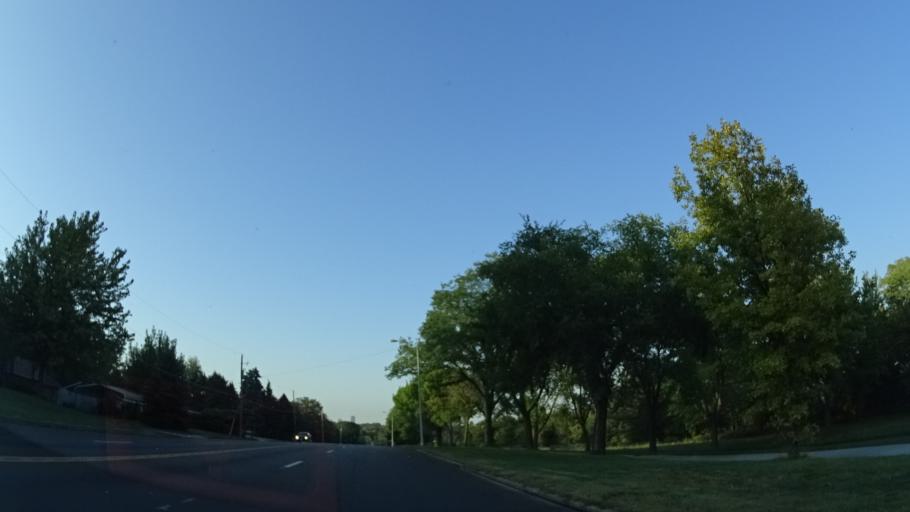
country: US
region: Nebraska
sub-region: Douglas County
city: Omaha
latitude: 41.2033
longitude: -95.9336
